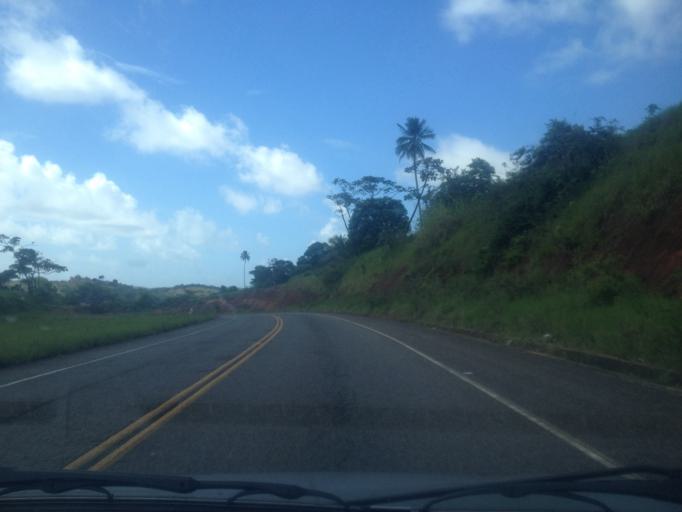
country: BR
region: Bahia
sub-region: Conde
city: Conde
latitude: -12.0572
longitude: -37.7226
